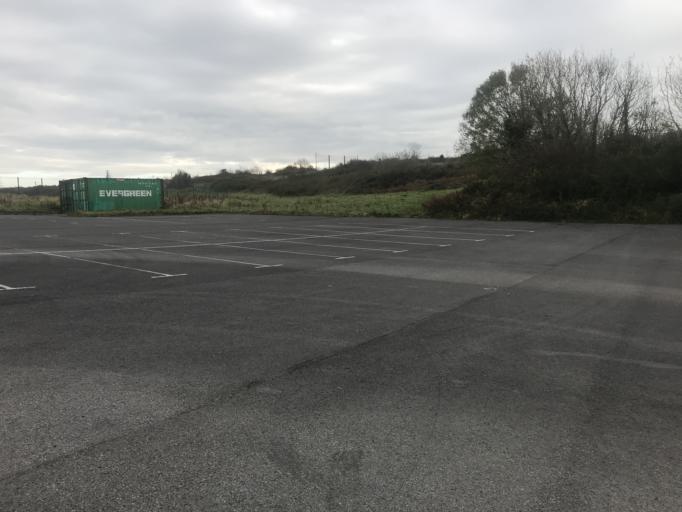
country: IE
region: Connaught
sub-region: County Galway
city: Gaillimh
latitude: 53.2932
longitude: -9.0487
